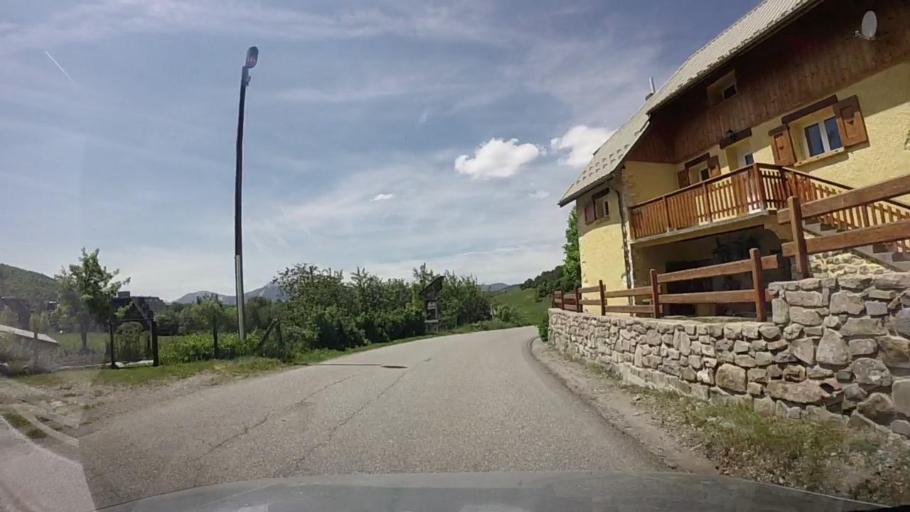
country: FR
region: Provence-Alpes-Cote d'Azur
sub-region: Departement des Alpes-de-Haute-Provence
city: Seyne-les-Alpes
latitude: 44.4151
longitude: 6.3507
